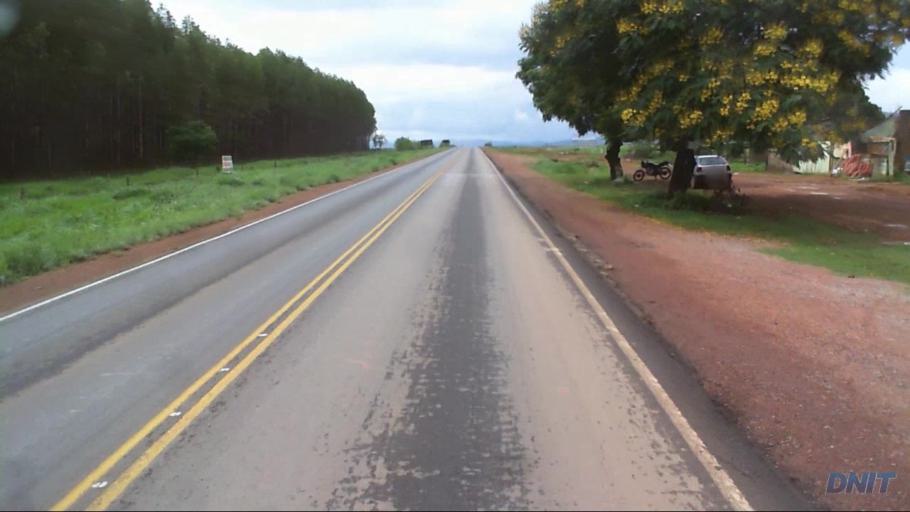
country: BR
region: Goias
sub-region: Padre Bernardo
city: Padre Bernardo
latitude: -15.2668
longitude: -48.2638
